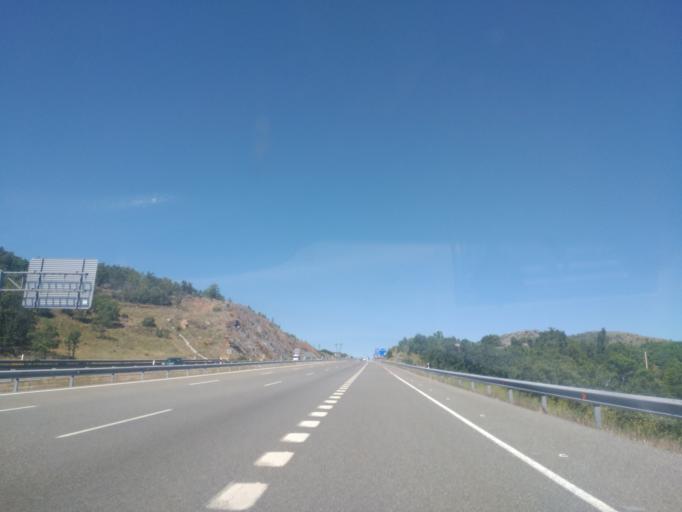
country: ES
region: Castille and Leon
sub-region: Provincia de Salamanca
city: Vallejera de Riofrio
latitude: 40.4009
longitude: -5.7340
